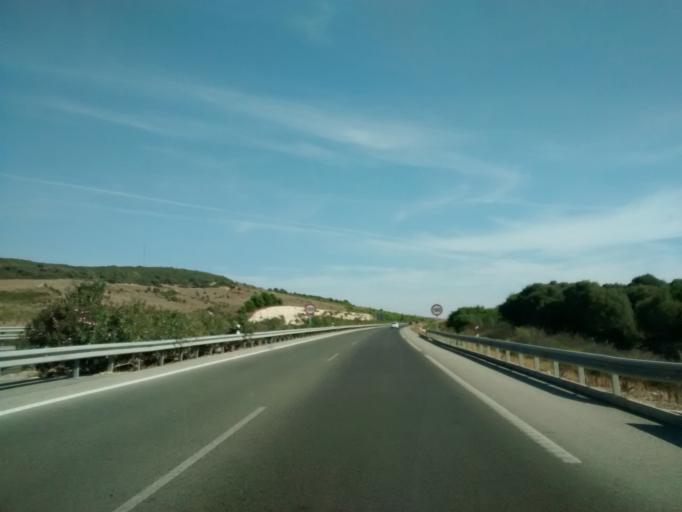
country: ES
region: Andalusia
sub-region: Provincia de Cadiz
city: Conil de la Frontera
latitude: 36.3186
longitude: -6.0571
